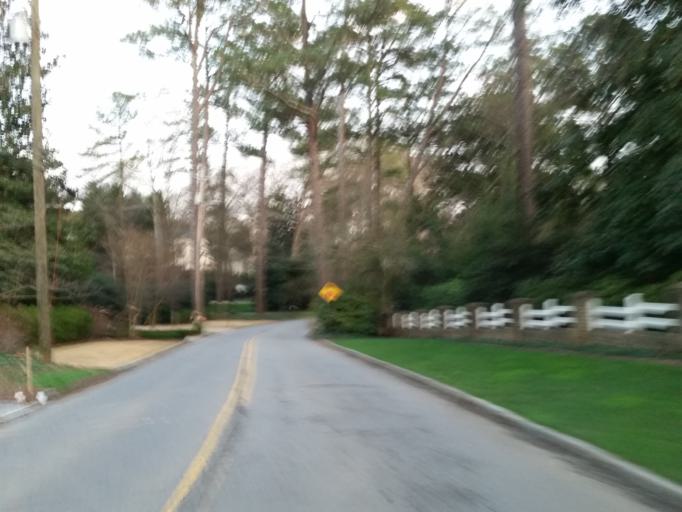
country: US
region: Georgia
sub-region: DeKalb County
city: North Atlanta
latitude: 33.8588
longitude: -84.3923
